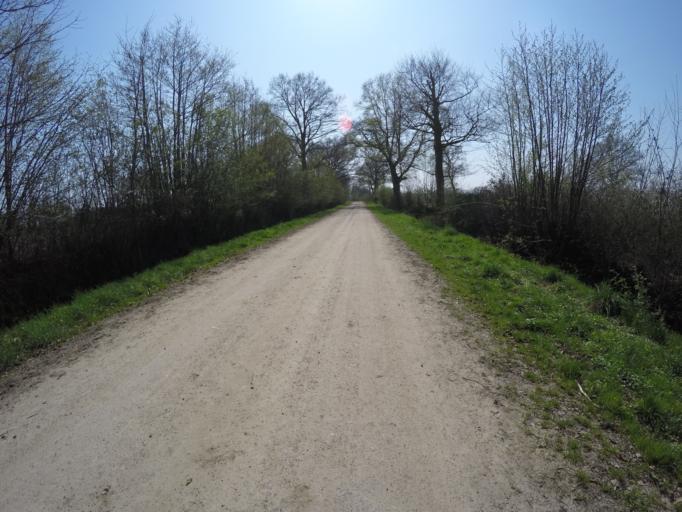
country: DE
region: Schleswig-Holstein
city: Borstel-Hohenraden
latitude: 53.7147
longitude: 9.8296
